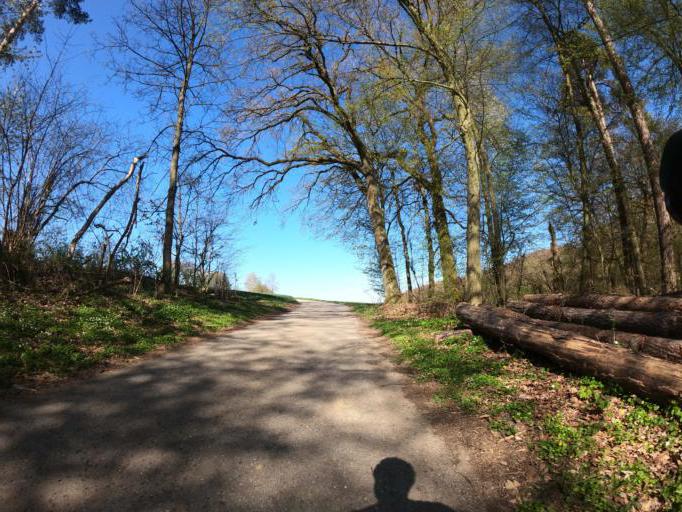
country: DE
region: Baden-Wuerttemberg
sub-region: Karlsruhe Region
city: Wiernsheim
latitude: 48.9107
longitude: 8.8703
